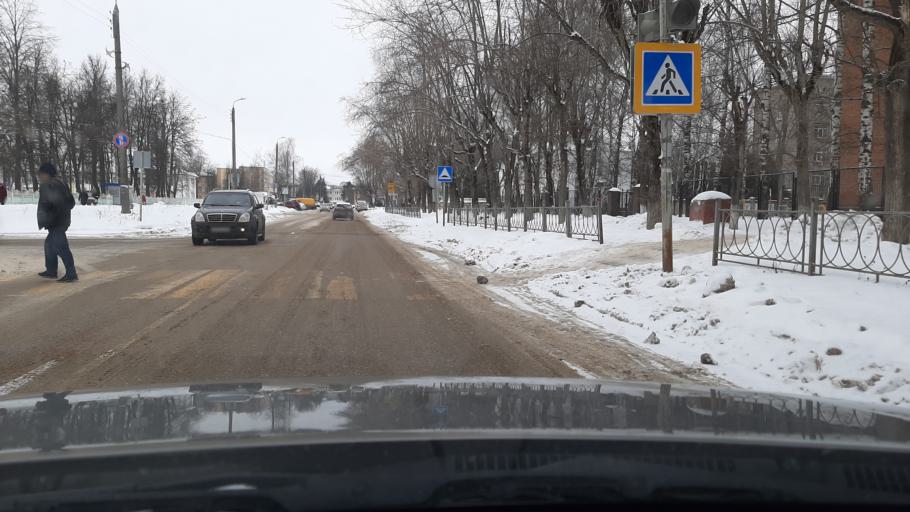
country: RU
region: Ivanovo
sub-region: Gorod Ivanovo
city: Ivanovo
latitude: 56.9721
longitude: 40.9688
